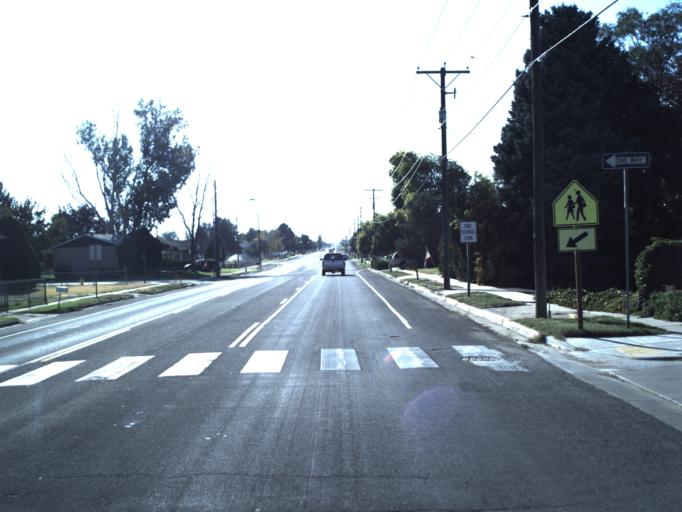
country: US
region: Utah
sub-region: Davis County
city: West Point
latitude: 41.1399
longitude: -112.0811
